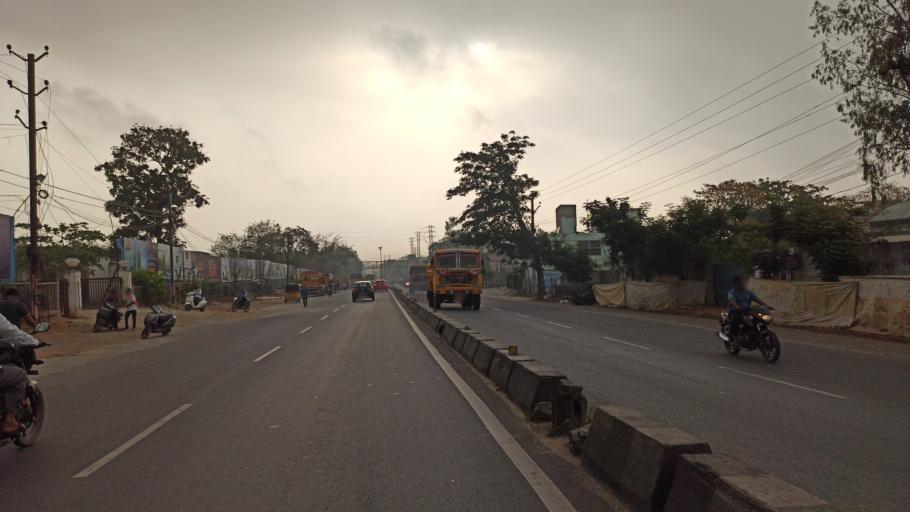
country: IN
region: Telangana
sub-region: Rangareddi
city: Uppal Kalan
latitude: 17.4014
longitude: 78.5473
